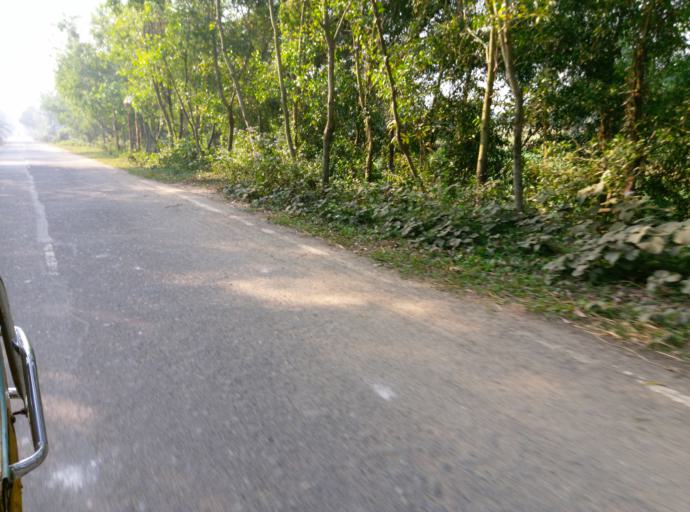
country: BD
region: Dhaka
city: Netrakona
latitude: 25.1366
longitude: 90.6617
